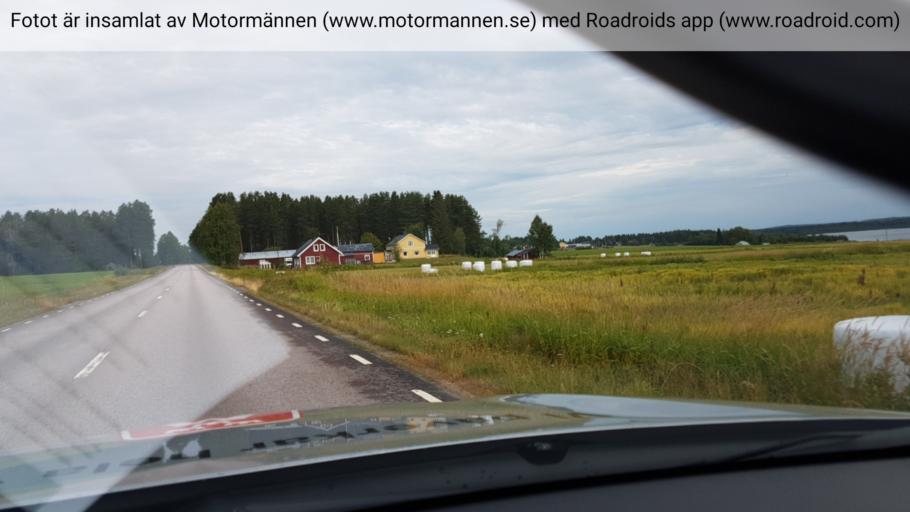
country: SE
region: Norrbotten
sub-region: Lulea Kommun
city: Sodra Sunderbyn
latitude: 65.6228
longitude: 21.9377
